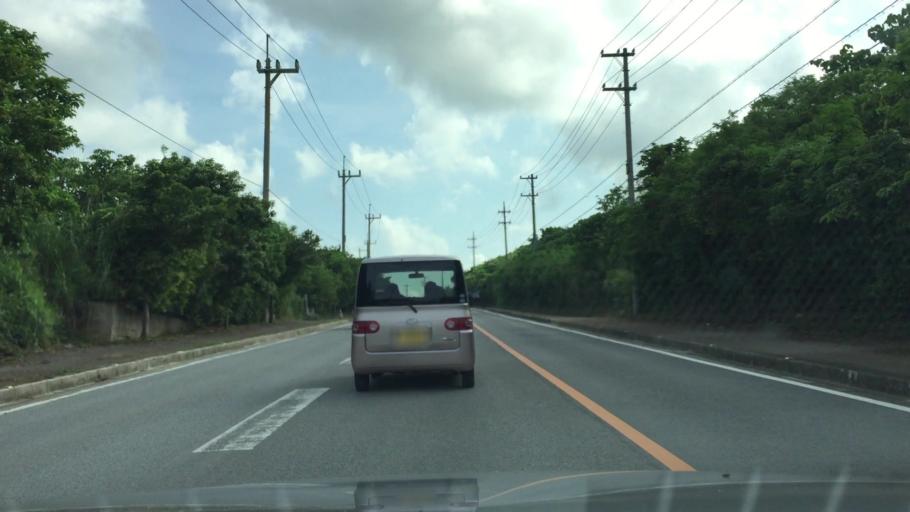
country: JP
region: Okinawa
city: Ishigaki
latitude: 24.4292
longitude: 124.2472
